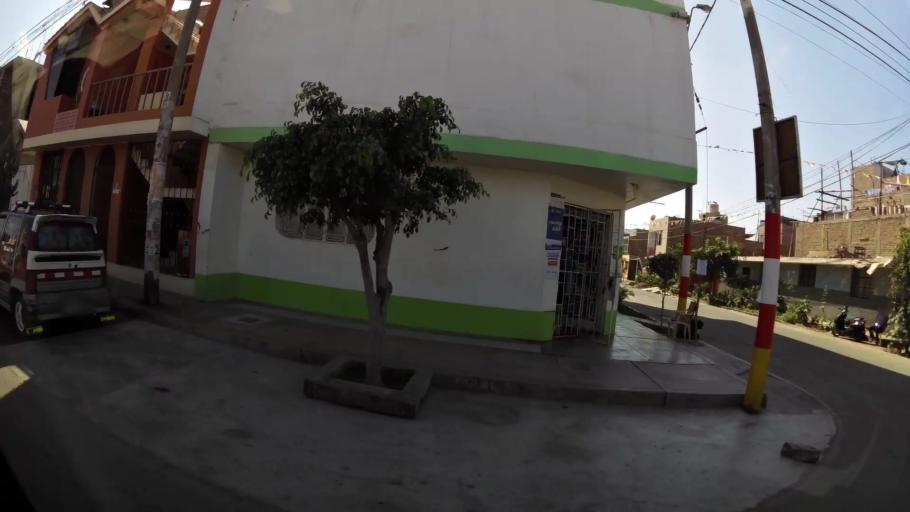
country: PE
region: Ica
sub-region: Provincia de Ica
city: Ica
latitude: -14.0653
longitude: -75.7226
